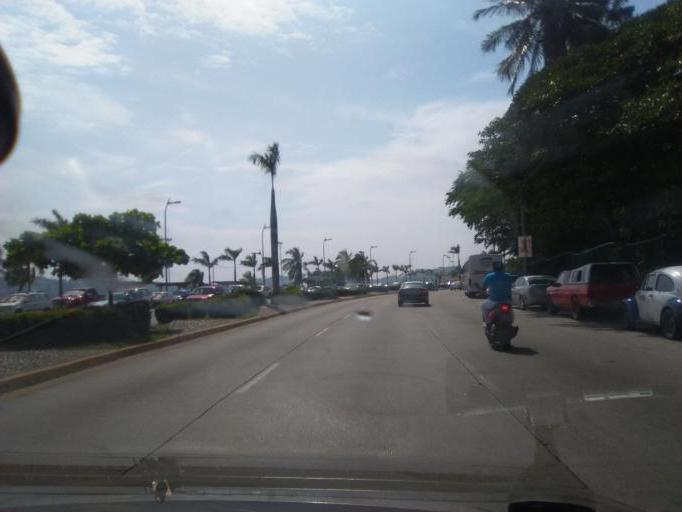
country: MX
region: Guerrero
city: Acapulco de Juarez
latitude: 16.8587
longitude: -99.8877
